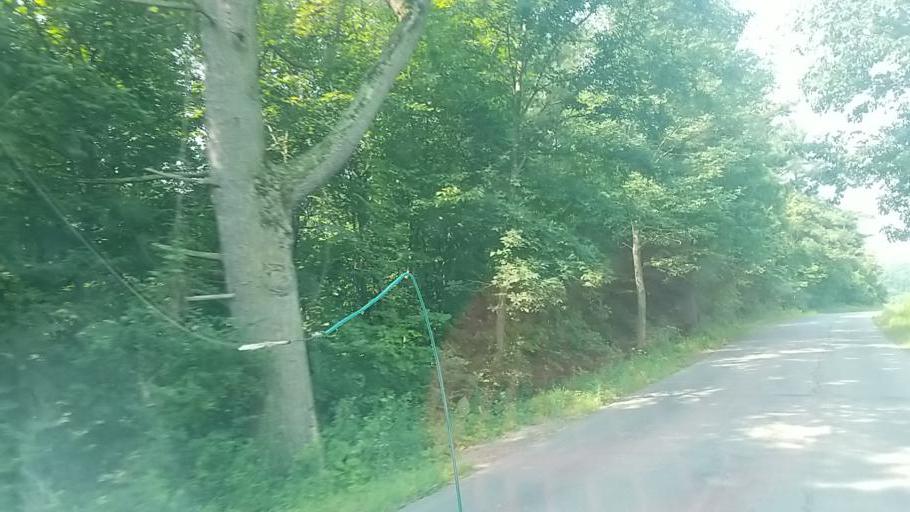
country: US
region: New York
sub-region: Montgomery County
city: Fonda
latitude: 42.9482
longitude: -74.4464
